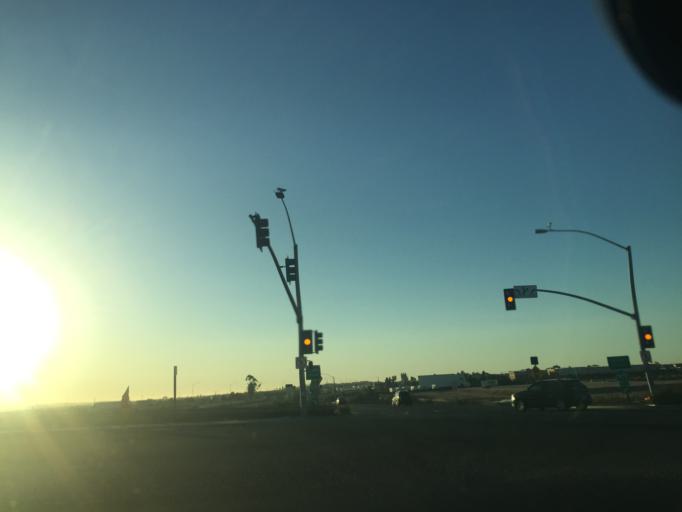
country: MX
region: Baja California
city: Tijuana
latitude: 32.5650
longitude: -116.9797
